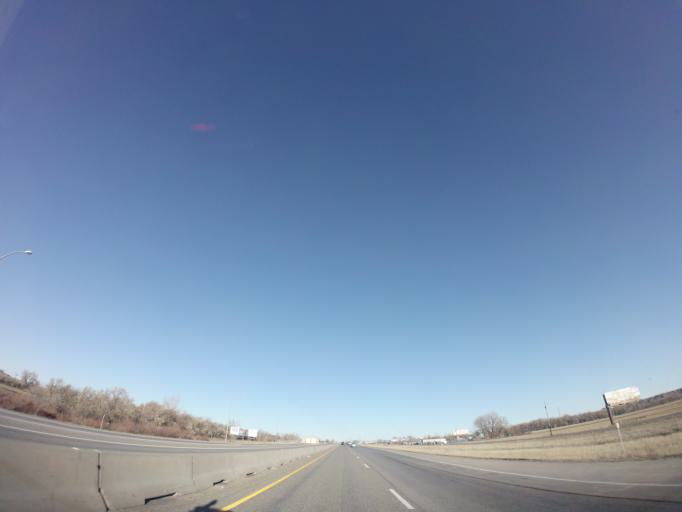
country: US
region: Montana
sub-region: Yellowstone County
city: Laurel
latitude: 45.6892
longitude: -108.6912
